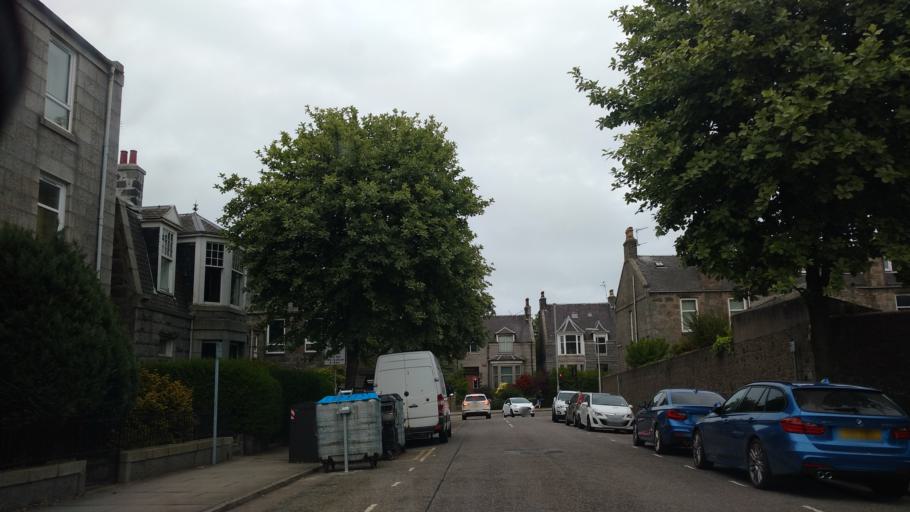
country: GB
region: Scotland
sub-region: Aberdeen City
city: Aberdeen
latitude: 57.1610
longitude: -2.0977
